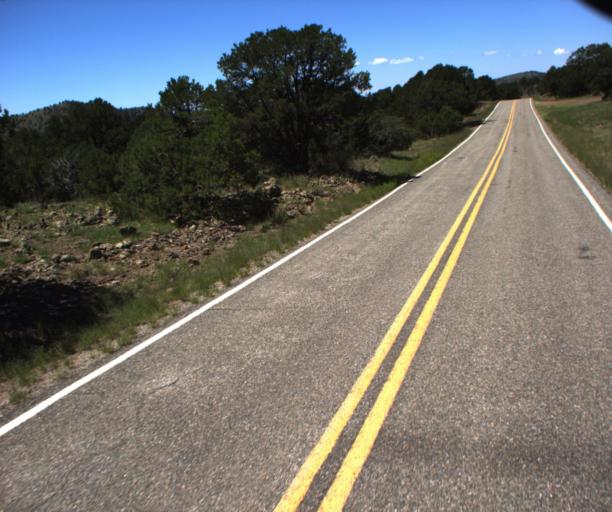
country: US
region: Arizona
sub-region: Greenlee County
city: Morenci
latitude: 33.3635
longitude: -109.3359
